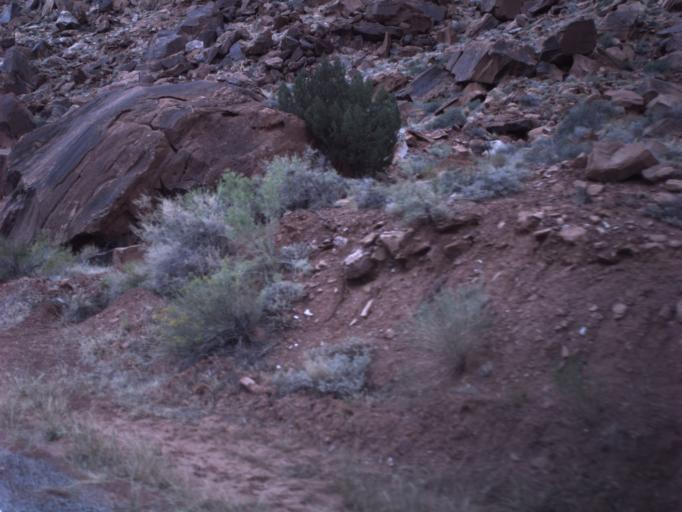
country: US
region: Utah
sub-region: Grand County
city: Moab
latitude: 38.7870
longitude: -109.3331
